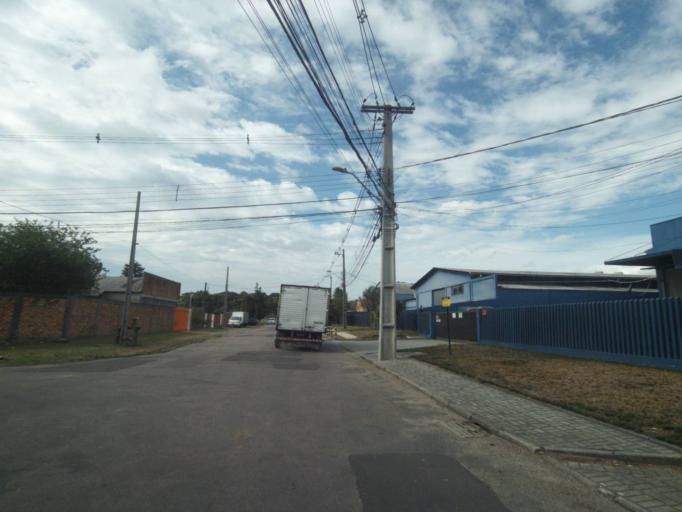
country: BR
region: Parana
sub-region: Curitiba
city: Curitiba
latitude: -25.4974
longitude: -49.3304
